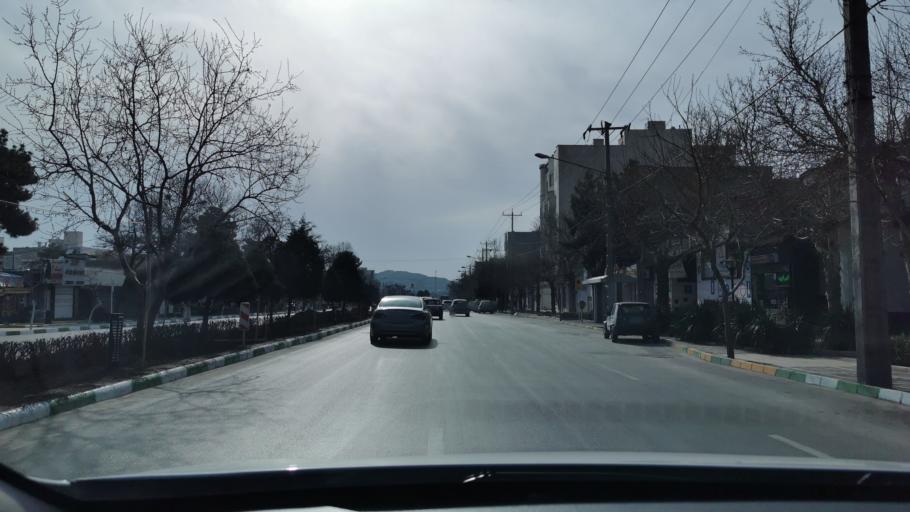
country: IR
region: Razavi Khorasan
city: Mashhad
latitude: 36.2871
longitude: 59.5443
